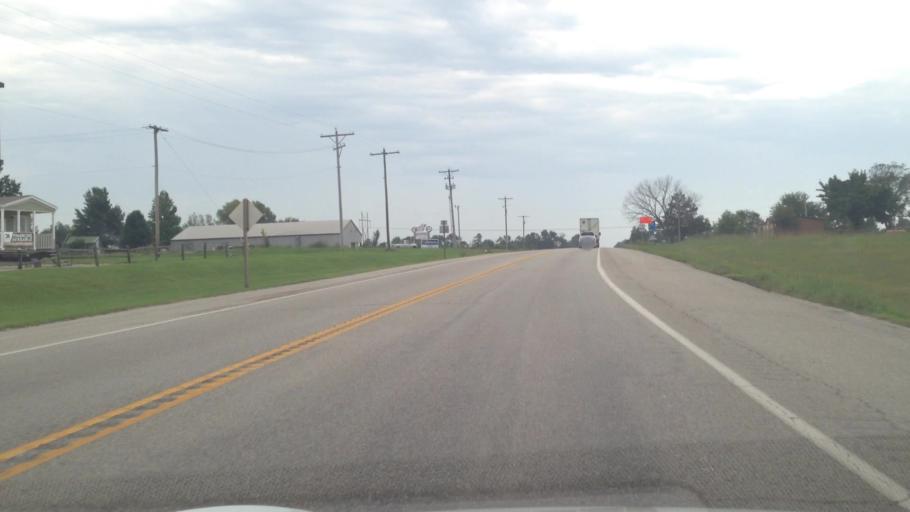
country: US
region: Kansas
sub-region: Crawford County
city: Pittsburg
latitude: 37.3364
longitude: -94.7054
